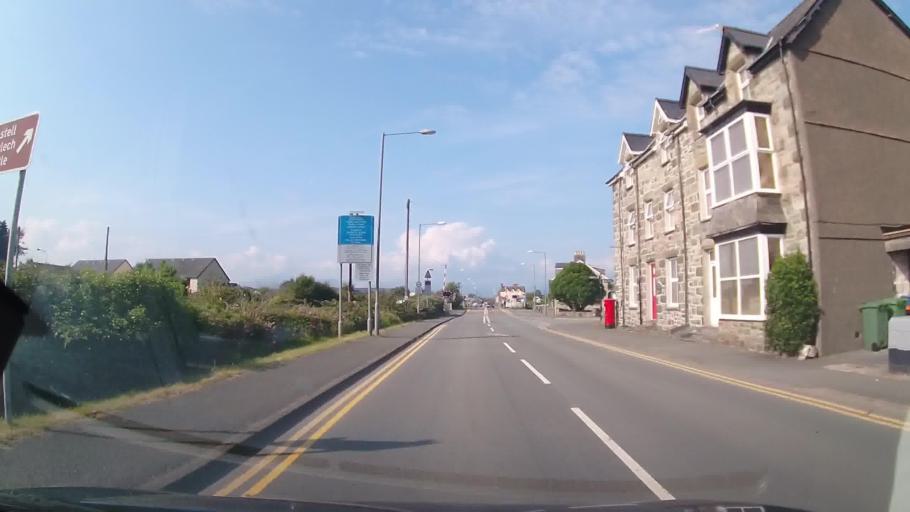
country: GB
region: Wales
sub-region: Gwynedd
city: Llanfair
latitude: 52.8590
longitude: -4.1113
